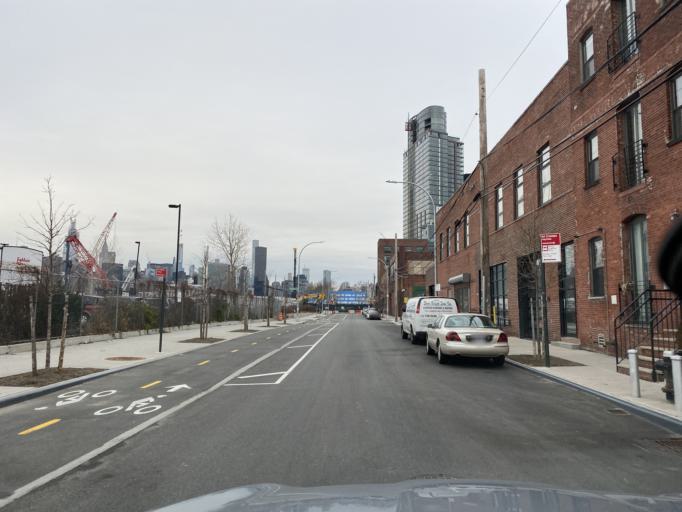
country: US
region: New York
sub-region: Queens County
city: Long Island City
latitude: 40.7333
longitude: -73.9598
